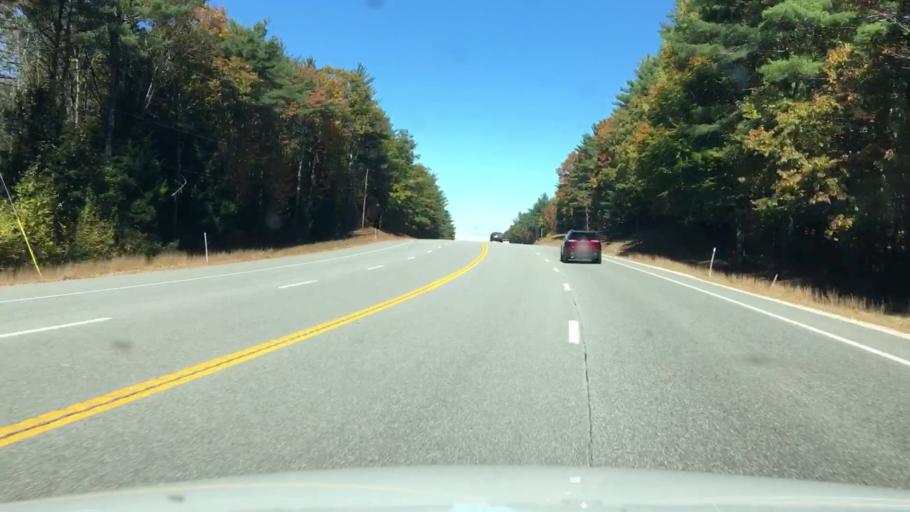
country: US
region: New Hampshire
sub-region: Carroll County
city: Ossipee
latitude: 43.6485
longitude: -71.0663
